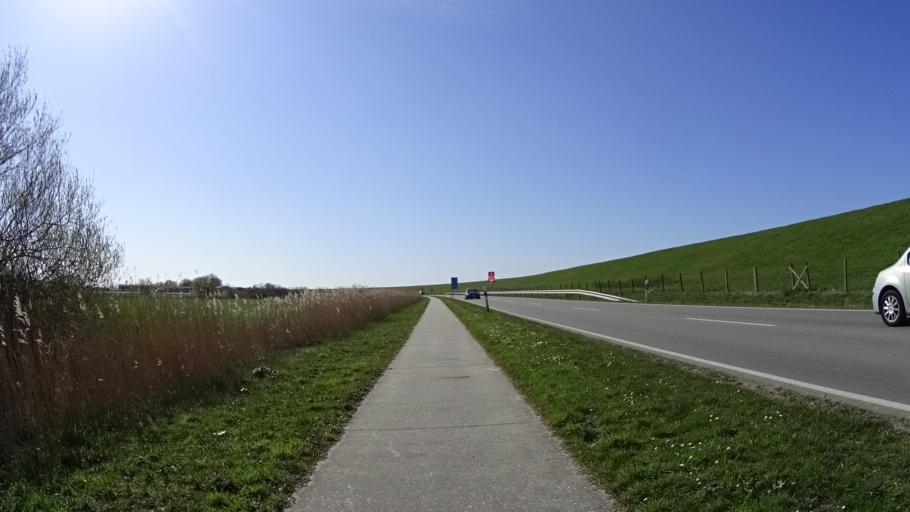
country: DE
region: Lower Saxony
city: Jemgum
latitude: 53.2402
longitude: 7.4073
